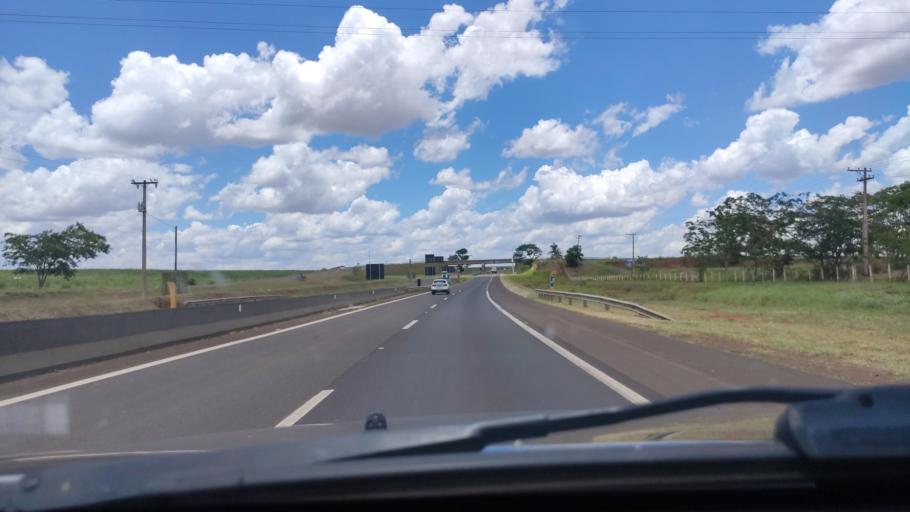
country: BR
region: Sao Paulo
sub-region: Pederneiras
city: Pederneiras
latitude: -22.3241
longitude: -48.7336
